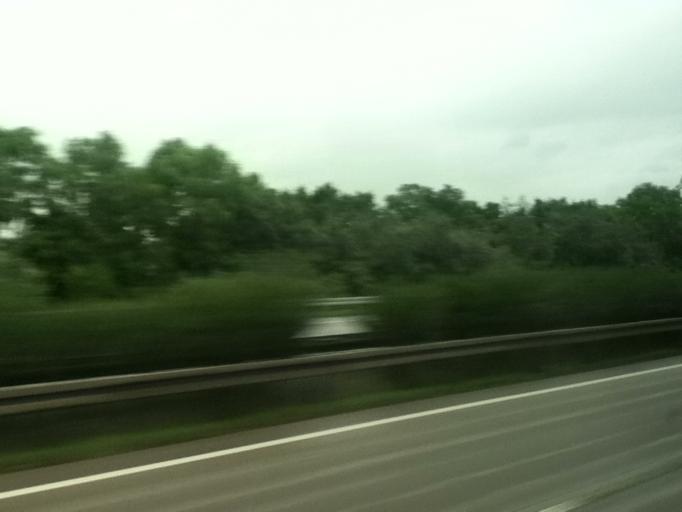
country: DE
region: Thuringia
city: Kirchheim
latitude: 50.9032
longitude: 10.9932
